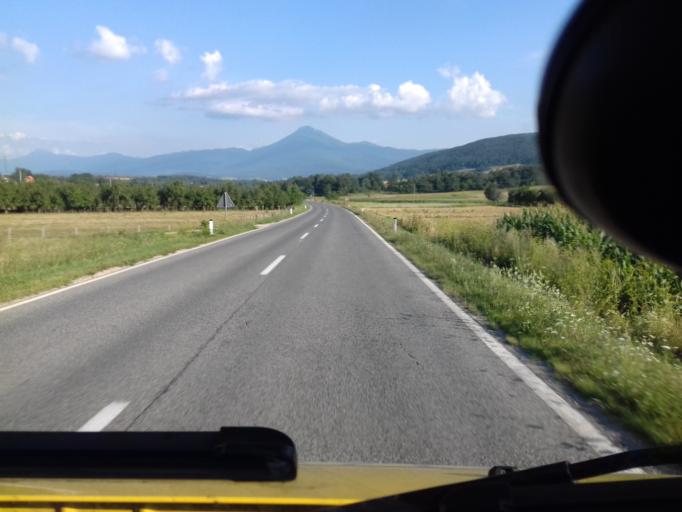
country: BA
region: Federation of Bosnia and Herzegovina
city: Orasac
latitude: 44.6450
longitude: 16.1666
